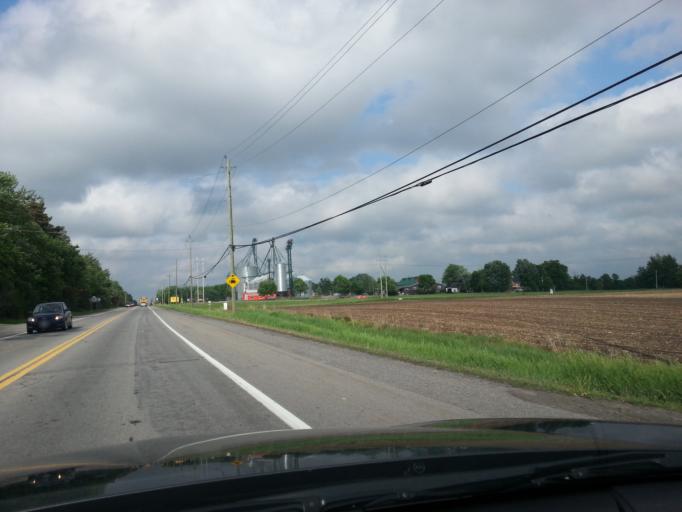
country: CA
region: Ontario
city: Bells Corners
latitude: 45.2649
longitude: -75.8150
